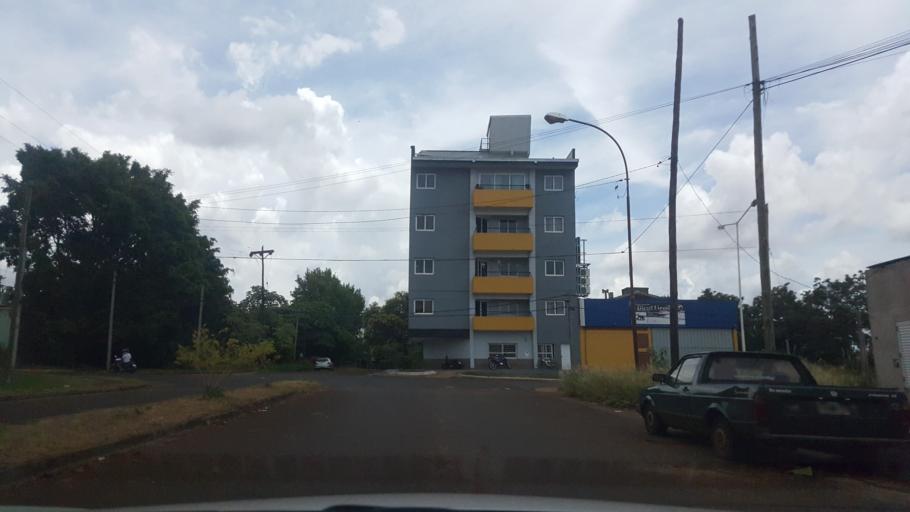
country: AR
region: Misiones
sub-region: Departamento de Capital
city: Posadas
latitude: -27.3991
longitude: -55.8934
